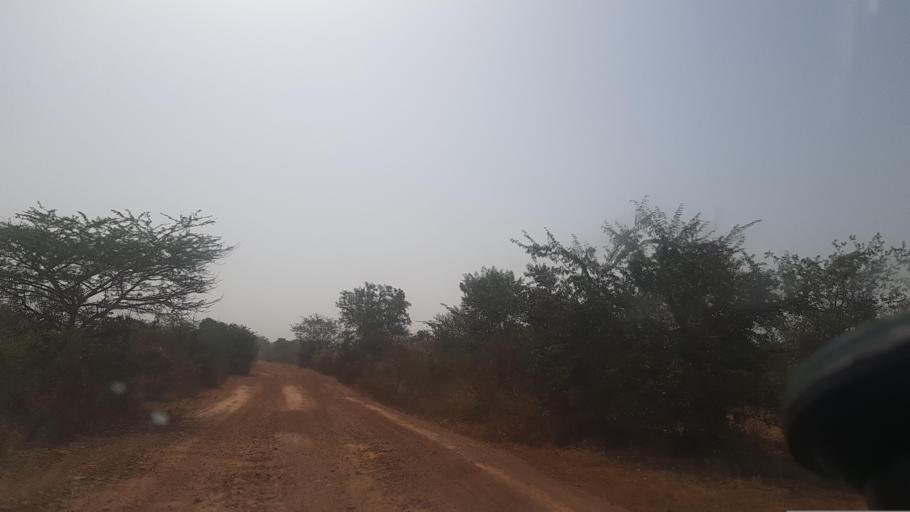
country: ML
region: Segou
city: Baroueli
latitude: 13.0783
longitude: -6.4850
